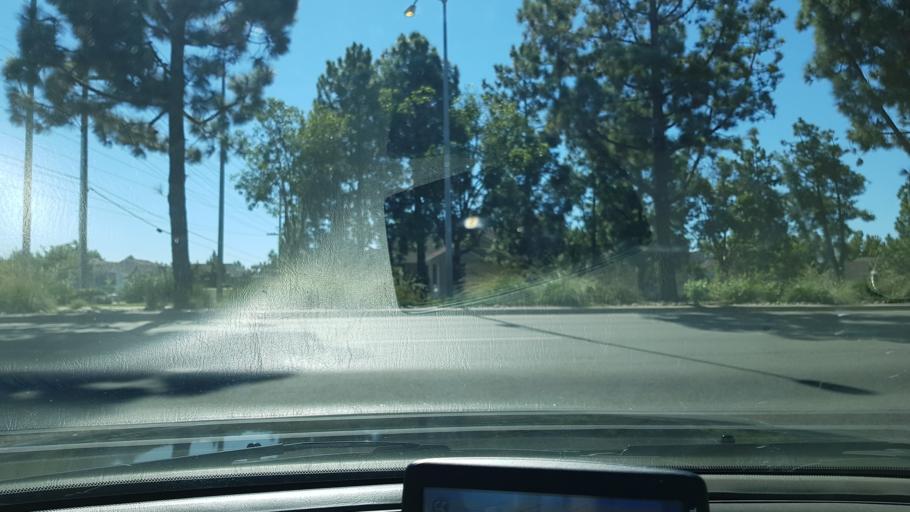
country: US
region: California
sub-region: San Diego County
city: Fairbanks Ranch
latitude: 32.9081
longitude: -117.1693
